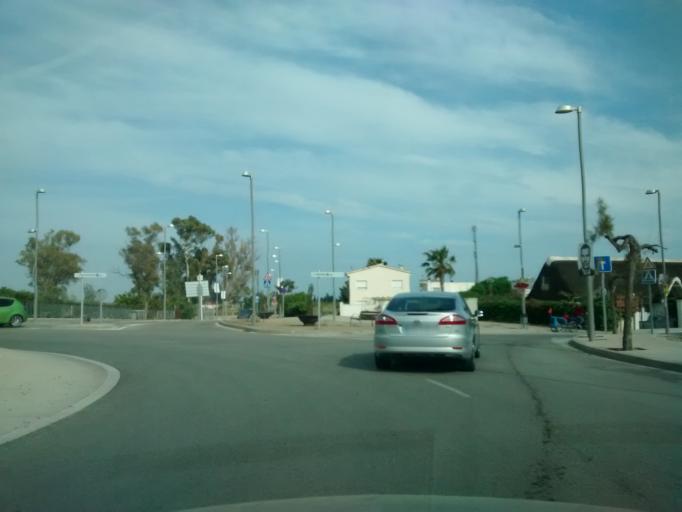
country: ES
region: Catalonia
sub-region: Provincia de Tarragona
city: Deltebre
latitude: 40.7111
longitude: 0.7166
